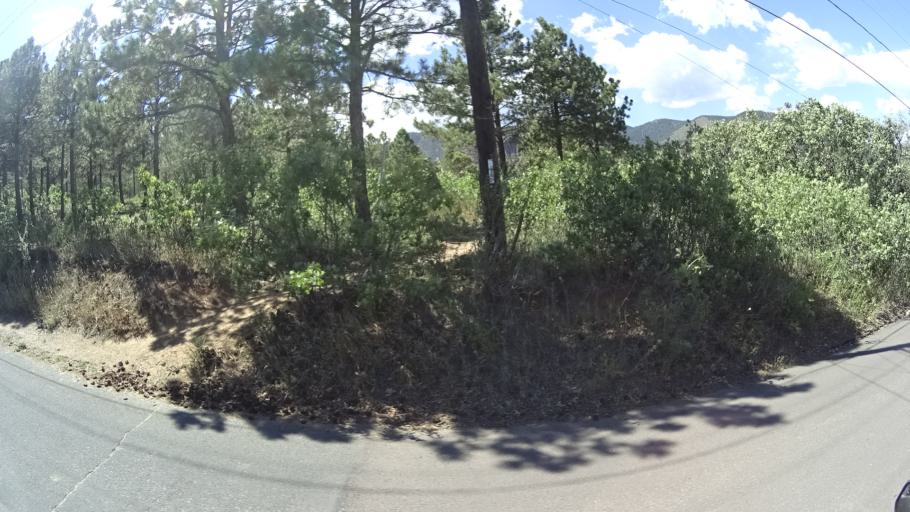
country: US
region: Colorado
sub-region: El Paso County
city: Colorado Springs
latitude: 38.7852
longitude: -104.8636
